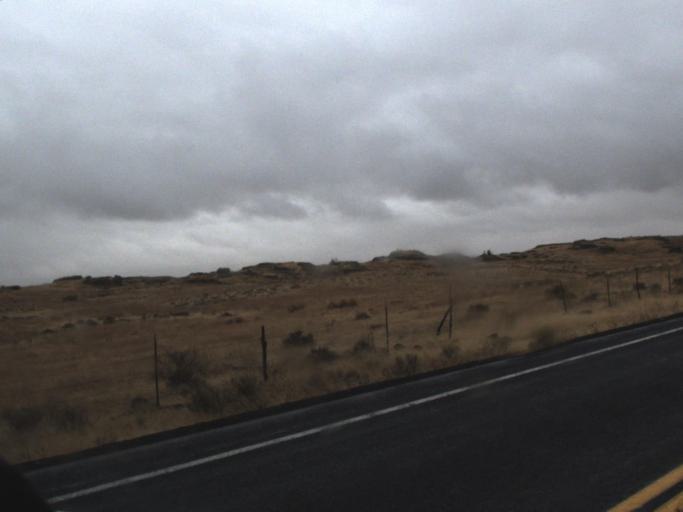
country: US
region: Washington
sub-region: Spokane County
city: Medical Lake
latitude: 47.2862
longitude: -117.9624
